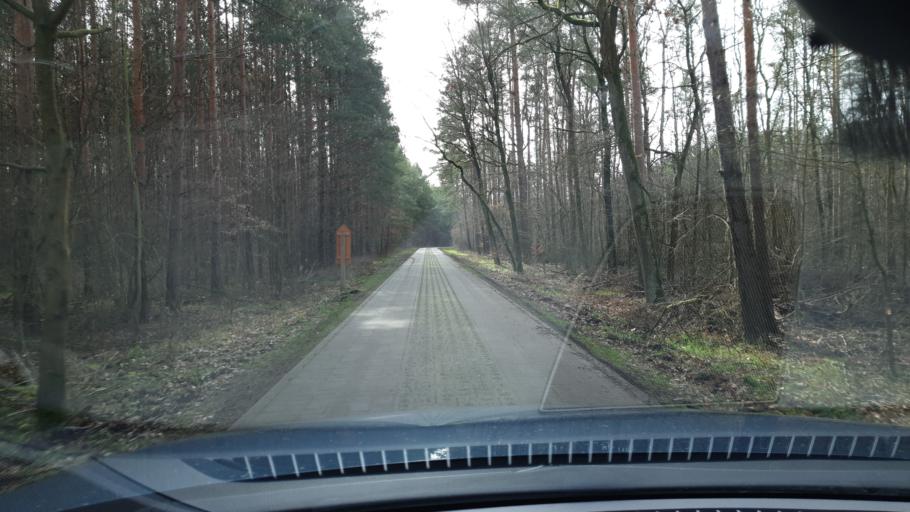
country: DE
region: Saxony-Anhalt
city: Vockerode
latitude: 51.8224
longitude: 12.3404
